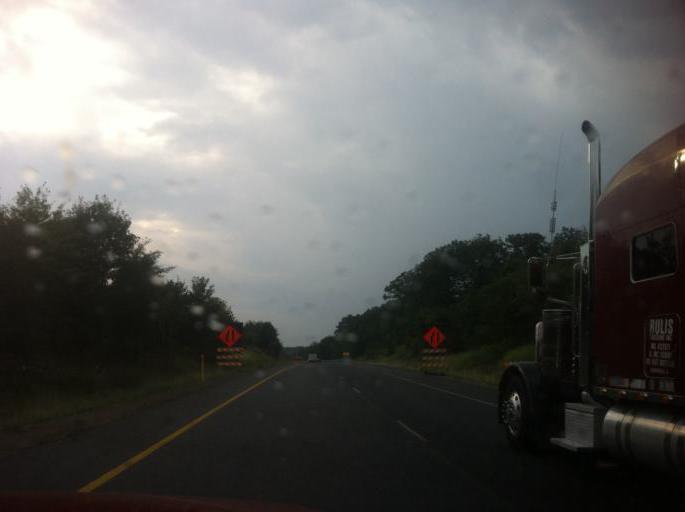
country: US
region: Pennsylvania
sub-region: Clarion County
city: Knox
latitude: 41.1974
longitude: -79.4816
